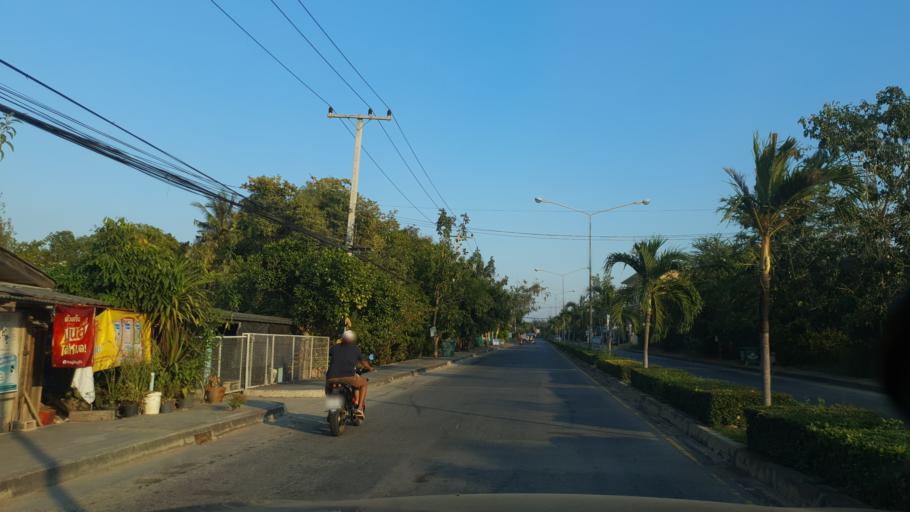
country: TH
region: Phetchaburi
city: Cha-am
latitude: 12.7800
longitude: 99.9704
